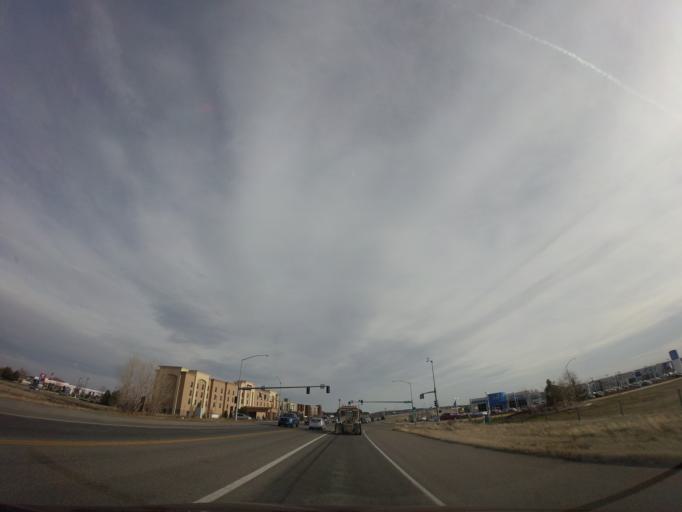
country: US
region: Montana
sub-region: Yellowstone County
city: Billings
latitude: 45.7356
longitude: -108.6101
